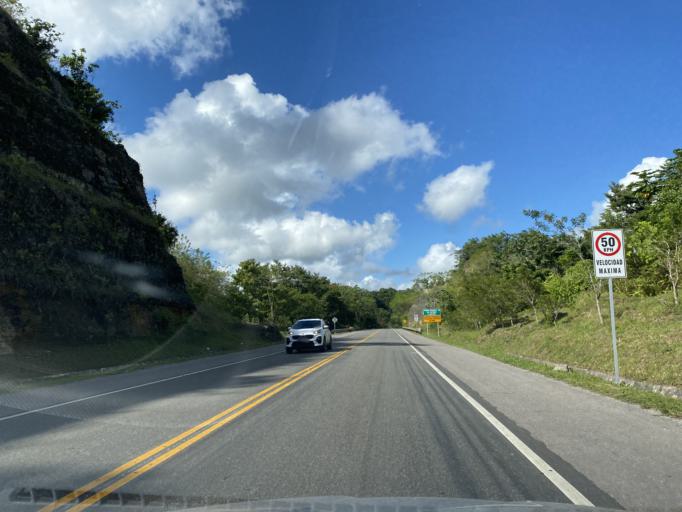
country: DO
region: Monte Plata
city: Majagual
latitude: 19.0442
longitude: -69.8309
